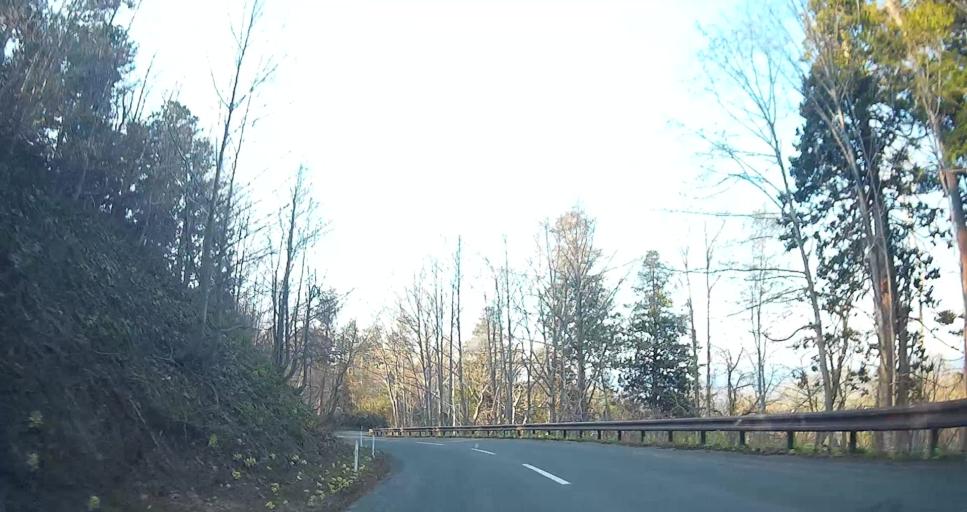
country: JP
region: Aomori
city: Mutsu
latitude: 41.3123
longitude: 141.1089
